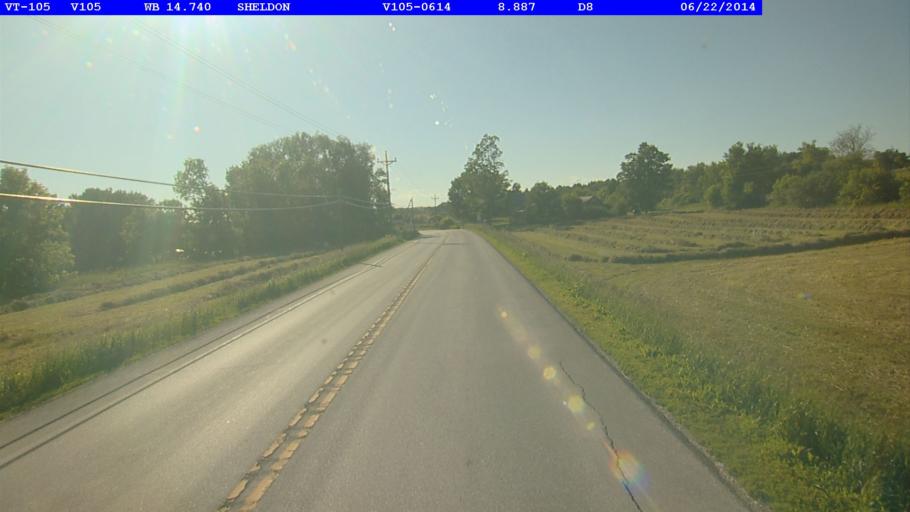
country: US
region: Vermont
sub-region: Franklin County
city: Enosburg Falls
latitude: 44.9103
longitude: -72.8623
